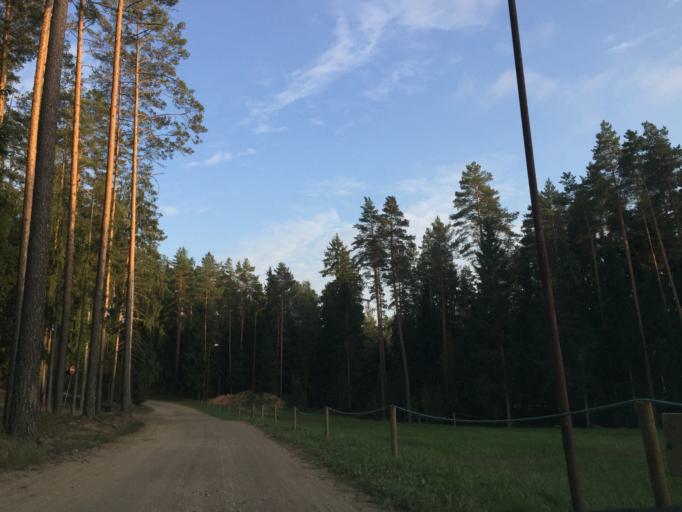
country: LV
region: Baldone
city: Baldone
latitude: 56.7700
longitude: 24.4002
